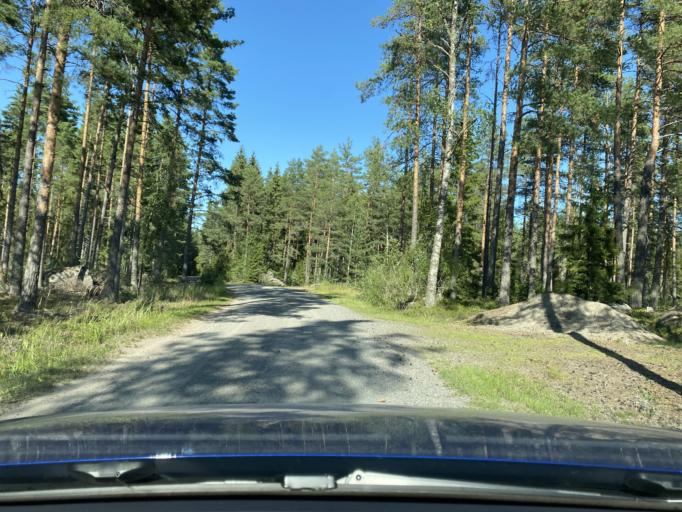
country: FI
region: Satakunta
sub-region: Rauma
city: Kiukainen
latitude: 61.1370
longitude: 22.0231
